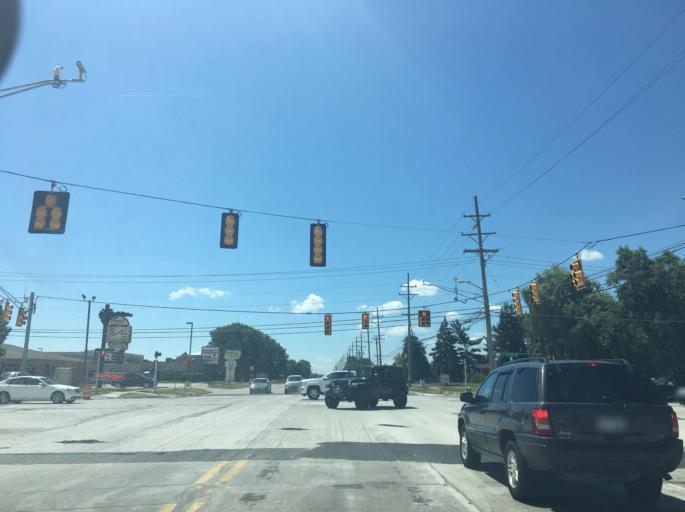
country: US
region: Michigan
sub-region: Macomb County
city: Clinton
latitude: 42.6133
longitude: -82.9529
